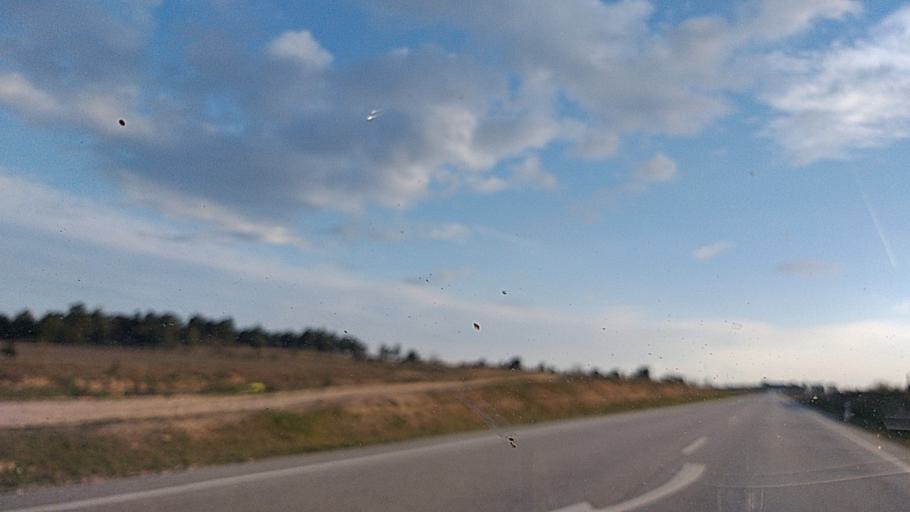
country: PT
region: Guarda
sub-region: Pinhel
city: Pinhel
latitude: 40.6529
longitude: -6.9669
